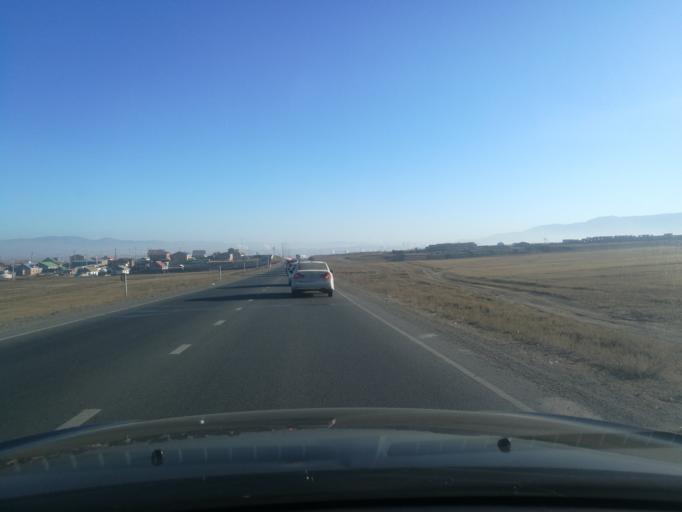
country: MN
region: Ulaanbaatar
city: Ulaanbaatar
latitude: 47.8413
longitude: 106.7236
